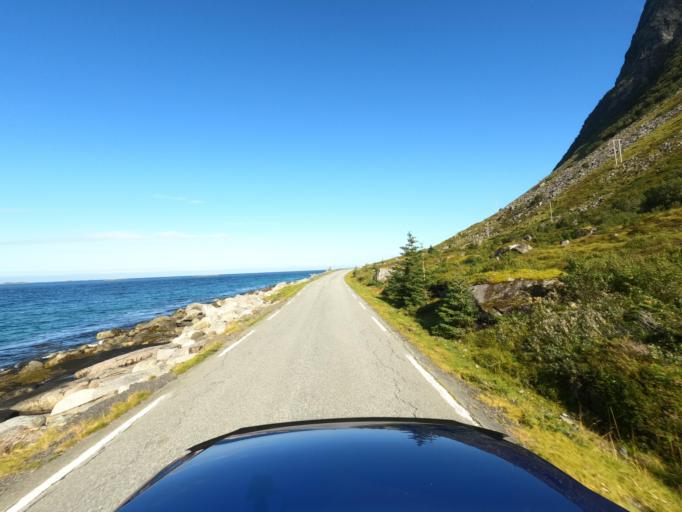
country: NO
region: Nordland
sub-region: Vagan
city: Kabelvag
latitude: 68.3161
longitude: 14.3098
